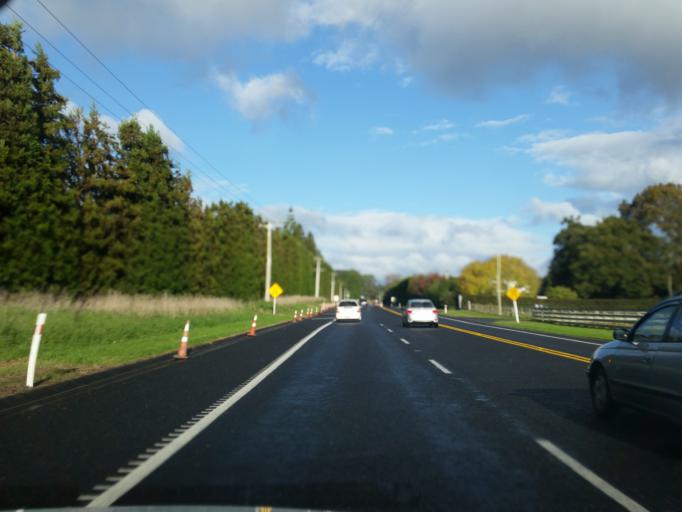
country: NZ
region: Bay of Plenty
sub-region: Western Bay of Plenty District
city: Katikati
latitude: -37.6218
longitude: 175.9520
